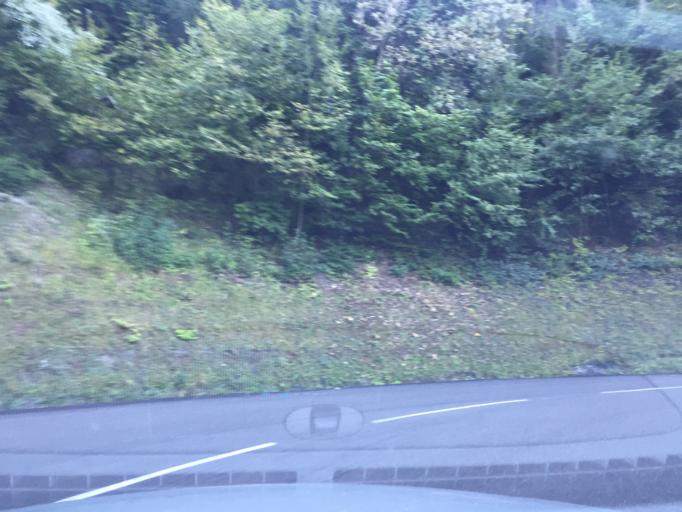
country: FR
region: Rhone-Alpes
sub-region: Departement de la Savoie
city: Bourg-Saint-Maurice
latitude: 45.5652
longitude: 6.7519
